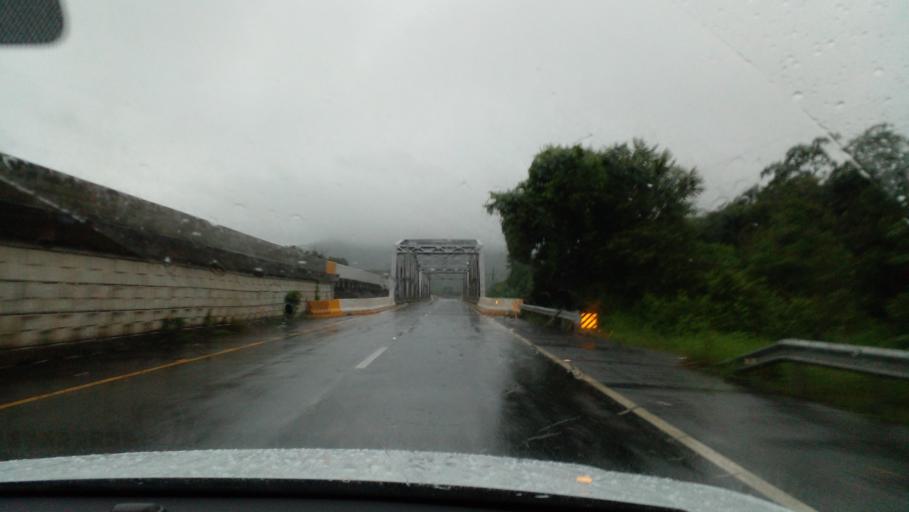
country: PA
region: Chiriqui
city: San Felix
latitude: 8.2799
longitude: -82.0496
